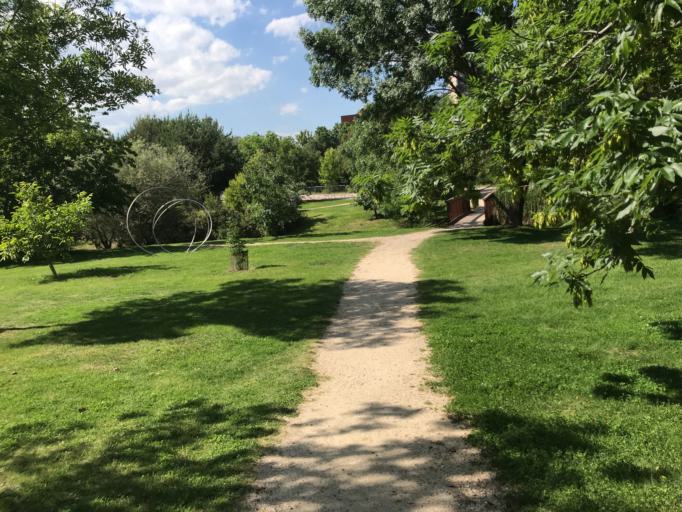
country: ES
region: Madrid
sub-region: Provincia de Madrid
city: Moncloa-Aravaca
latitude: 40.4464
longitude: -3.7264
